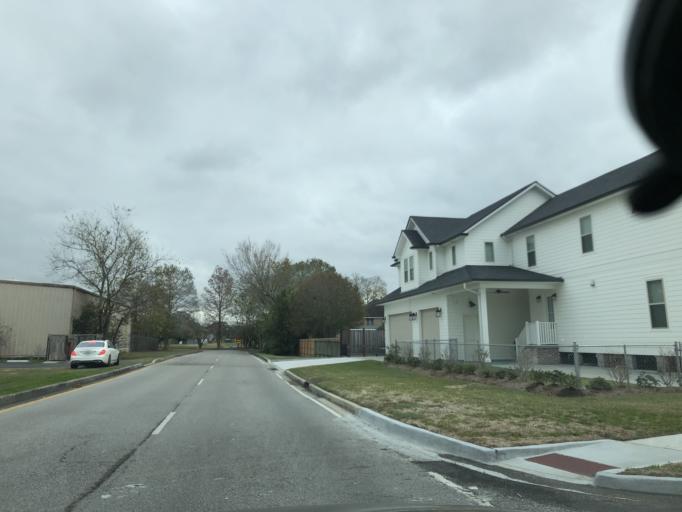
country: US
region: Louisiana
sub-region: Jefferson Parish
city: Metairie
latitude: 29.9920
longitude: -90.1540
